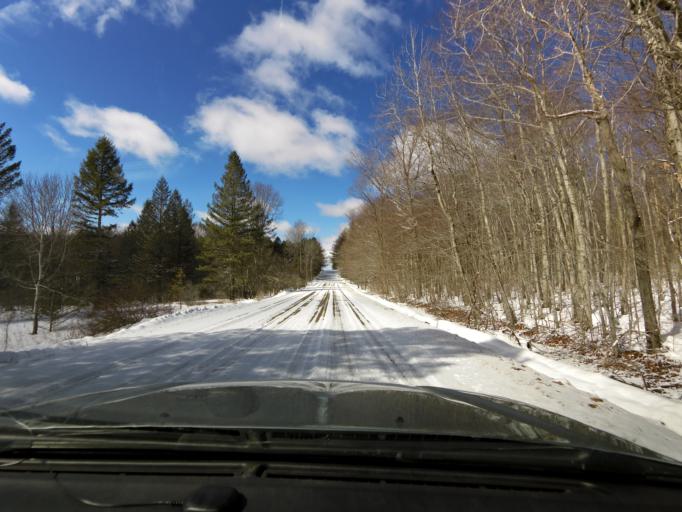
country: US
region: New York
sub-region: Cattaraugus County
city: Franklinville
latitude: 42.3428
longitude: -78.3929
